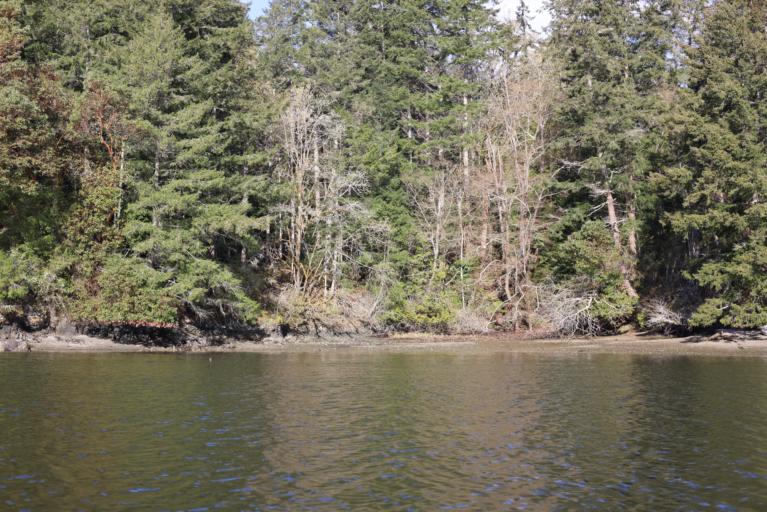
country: CA
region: British Columbia
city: North Saanich
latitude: 48.5714
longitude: -123.4748
